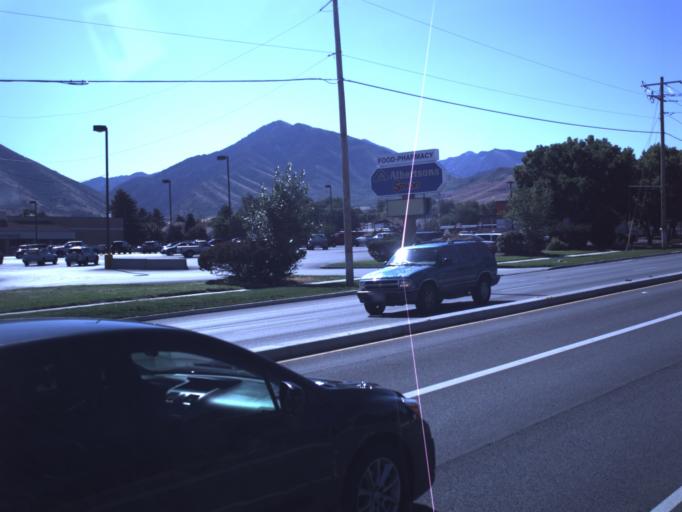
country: US
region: Utah
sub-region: Tooele County
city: Tooele
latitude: 40.5452
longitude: -112.2984
